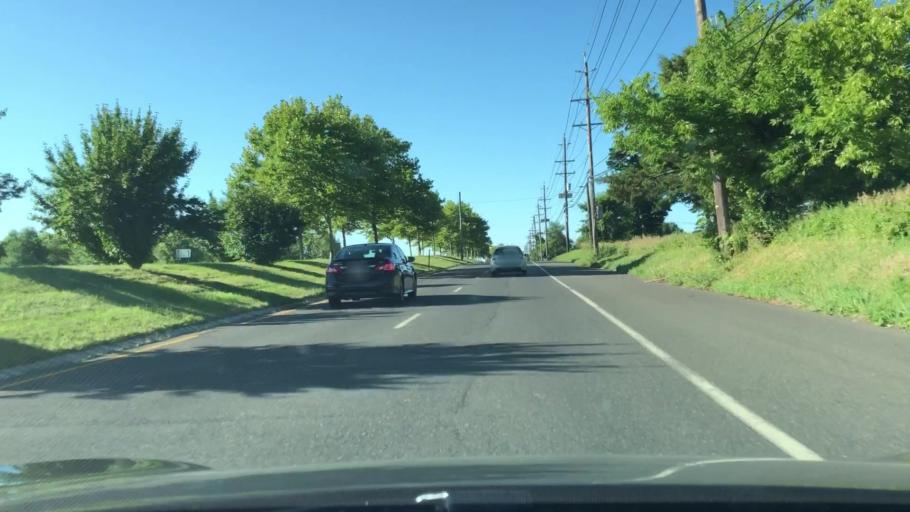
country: US
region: New Jersey
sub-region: Mercer County
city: Ewing
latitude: 40.3011
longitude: -74.8117
